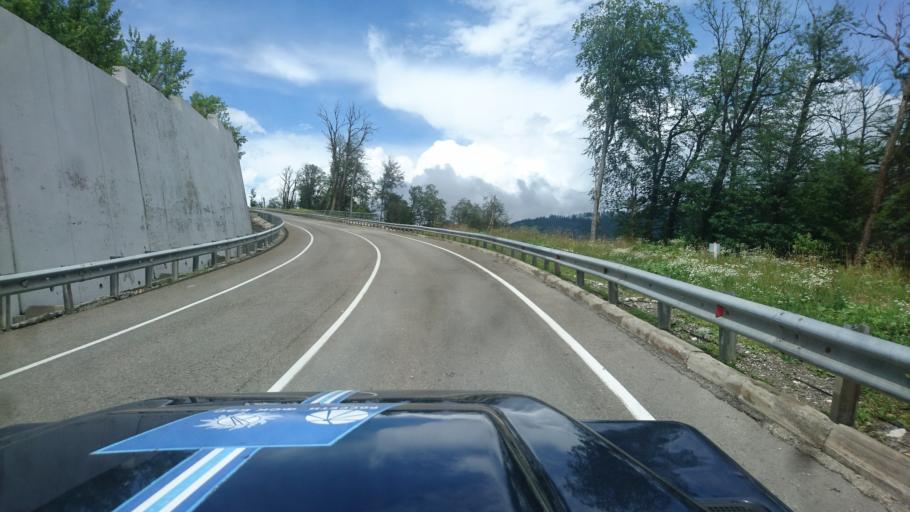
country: RU
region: Krasnodarskiy
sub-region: Sochi City
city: Krasnaya Polyana
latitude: 43.6586
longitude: 40.3271
